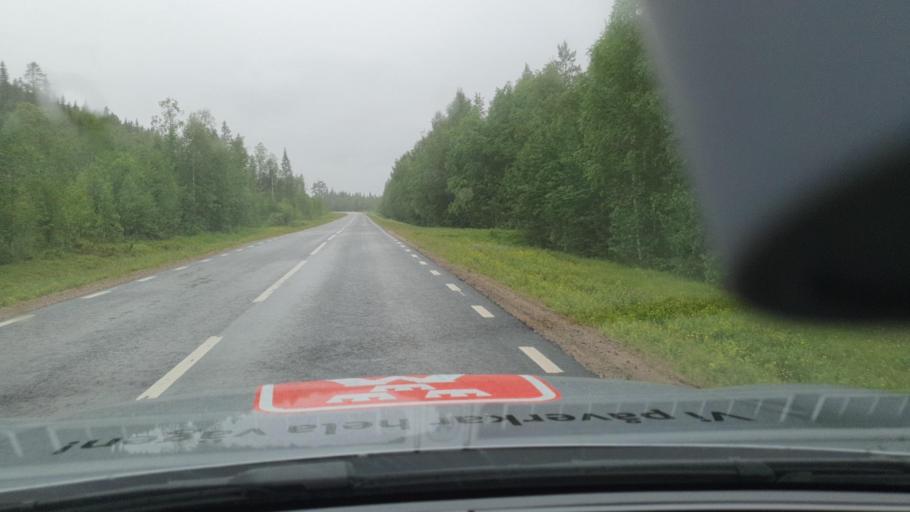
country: SE
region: Norrbotten
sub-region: Overtornea Kommun
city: OEvertornea
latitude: 66.4456
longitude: 23.3090
